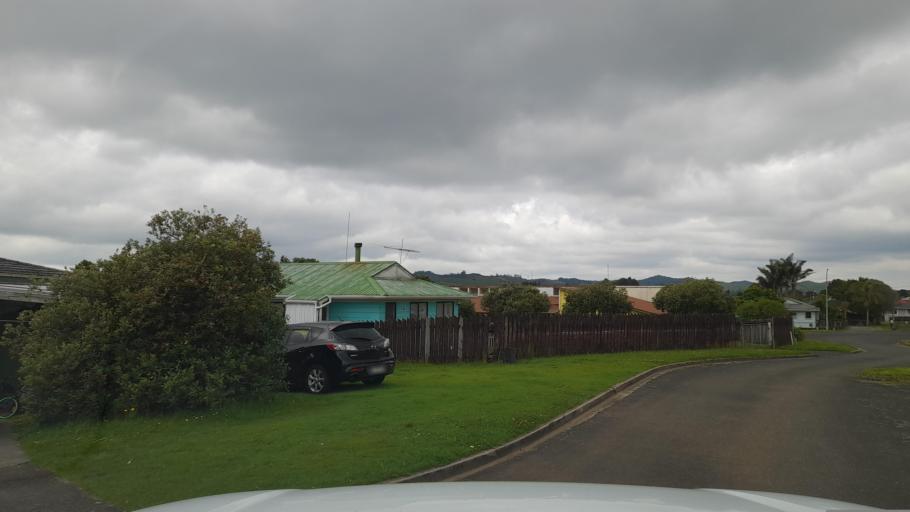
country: NZ
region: Northland
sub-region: Far North District
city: Waimate North
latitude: -35.4022
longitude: 173.7961
